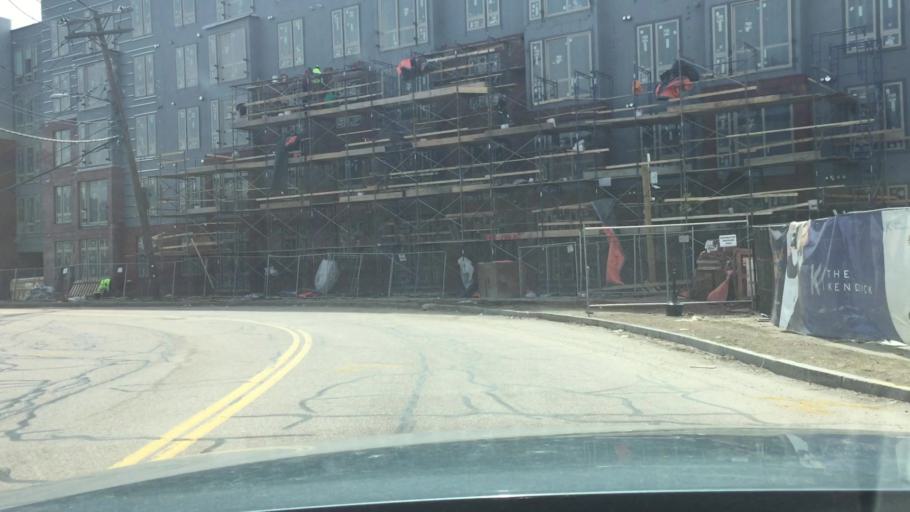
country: US
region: Massachusetts
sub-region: Norfolk County
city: Needham
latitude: 42.3023
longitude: -71.2155
